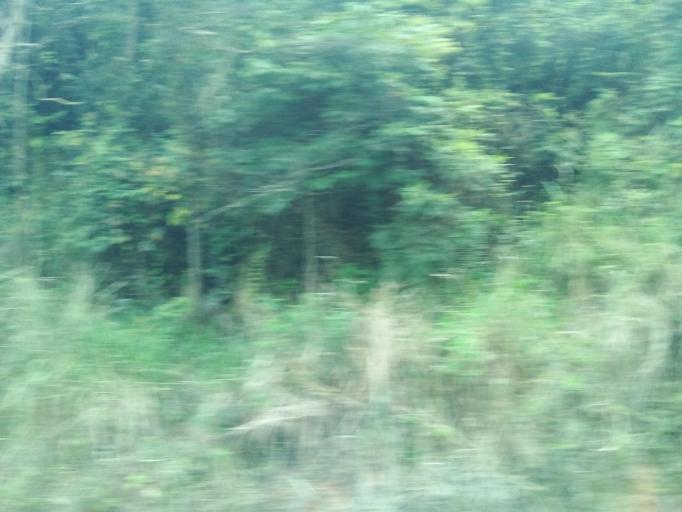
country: BR
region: Minas Gerais
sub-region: Joao Monlevade
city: Joao Monlevade
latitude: -19.8683
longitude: -43.1196
